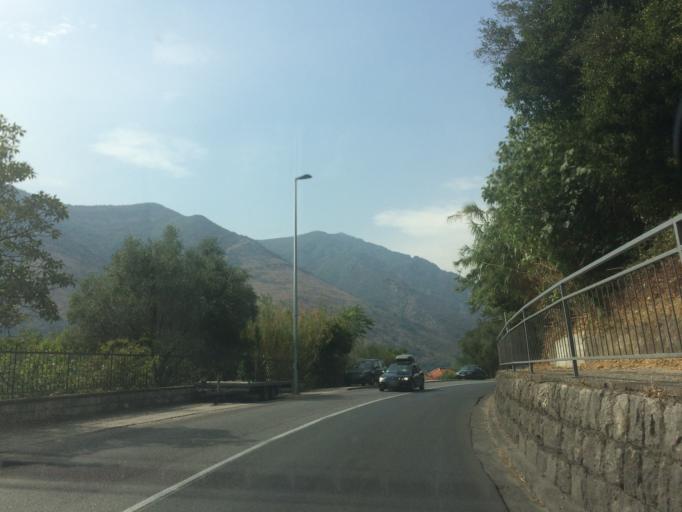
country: ME
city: Dobrota
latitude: 42.4394
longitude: 18.7642
